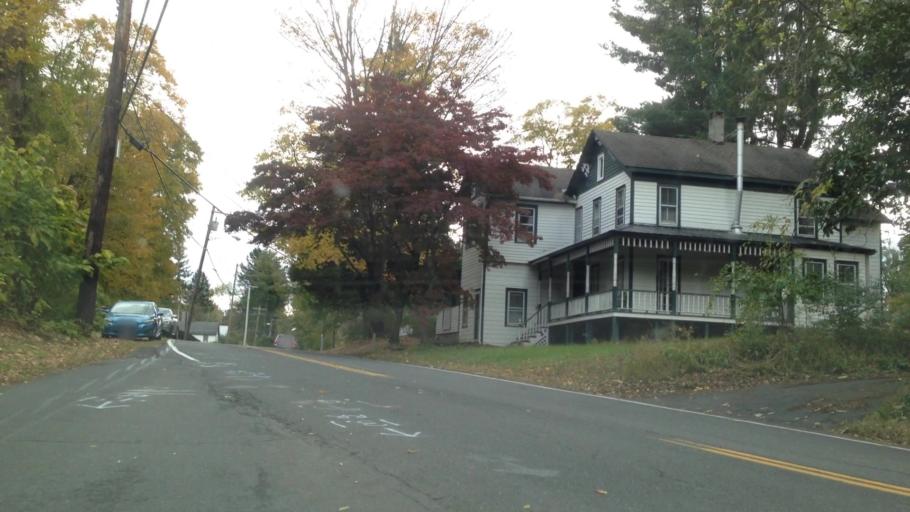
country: US
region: New York
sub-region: Ulster County
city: Rosendale Village
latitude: 41.8391
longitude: -74.0837
